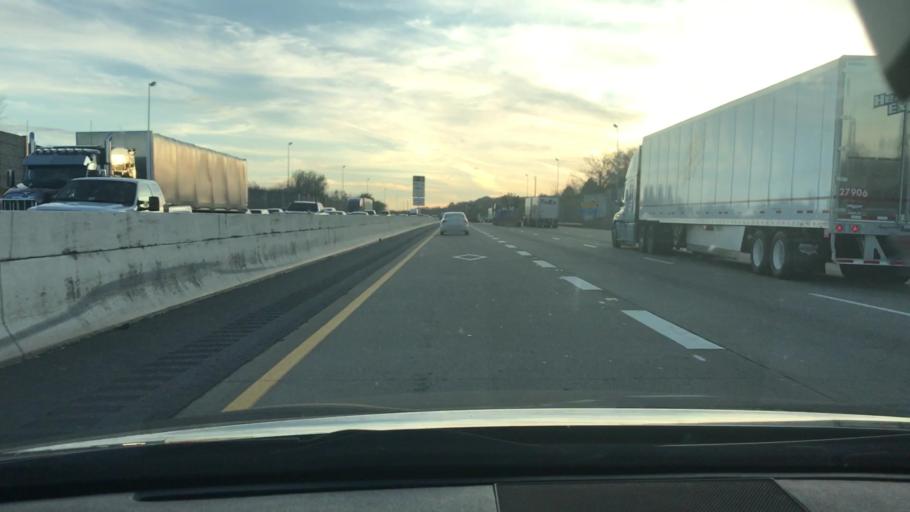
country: US
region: Tennessee
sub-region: Davidson County
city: Goodlettsville
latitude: 36.2862
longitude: -86.7275
